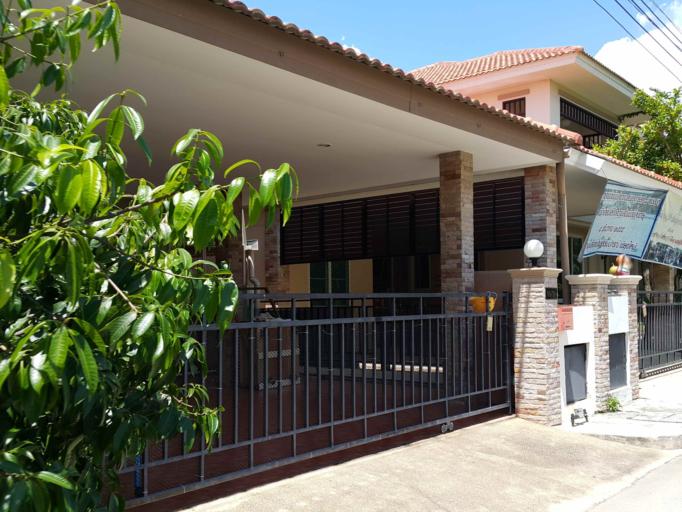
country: TH
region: Chiang Mai
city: Saraphi
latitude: 18.7577
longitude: 99.0418
